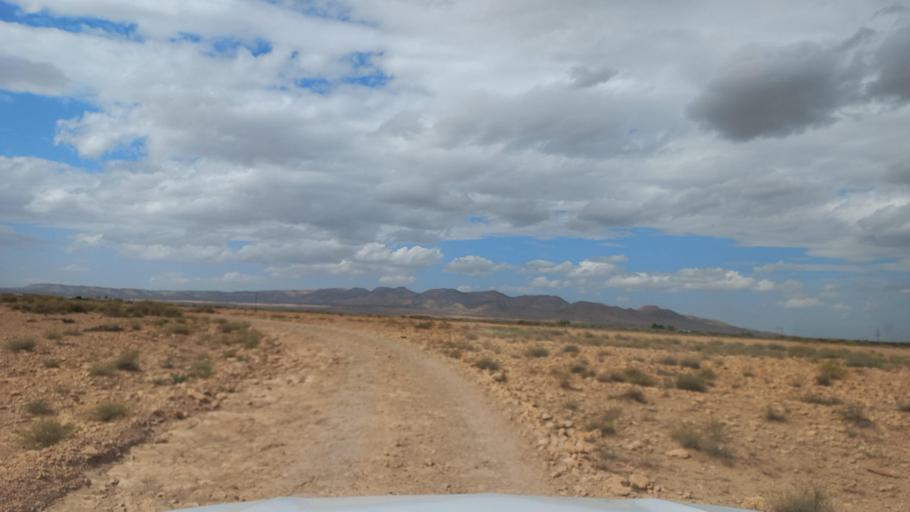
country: TN
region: Al Qasrayn
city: Sbiba
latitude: 35.3807
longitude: 9.1029
